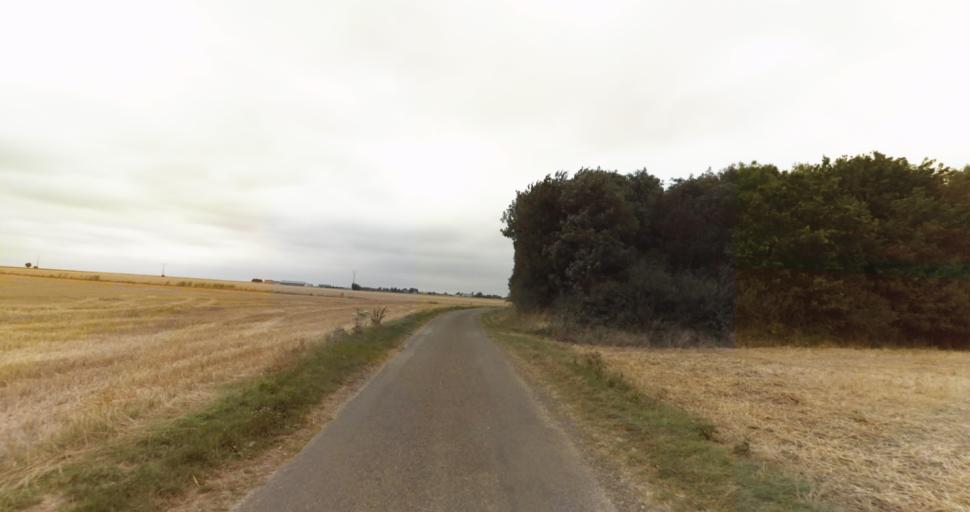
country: FR
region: Haute-Normandie
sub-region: Departement de l'Eure
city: La Couture-Boussey
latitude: 48.9235
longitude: 1.3600
